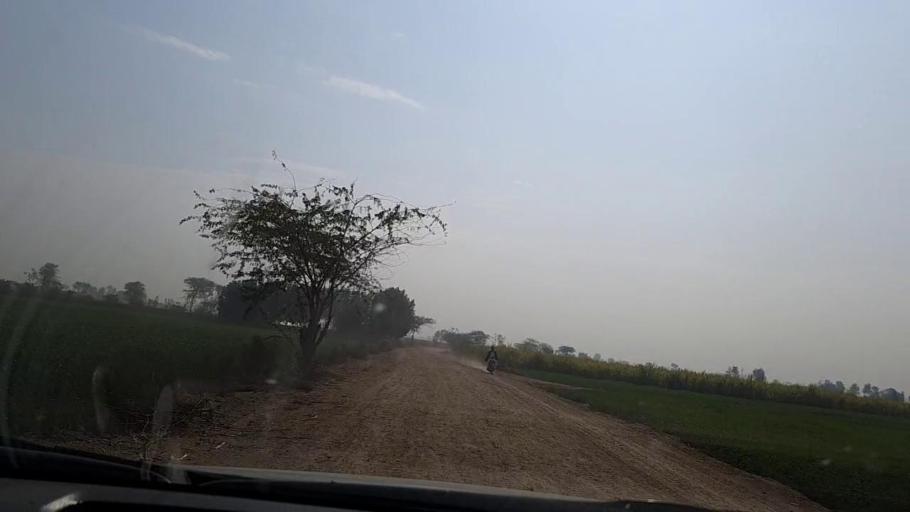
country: PK
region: Sindh
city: Daulatpur
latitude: 26.5464
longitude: 67.9859
